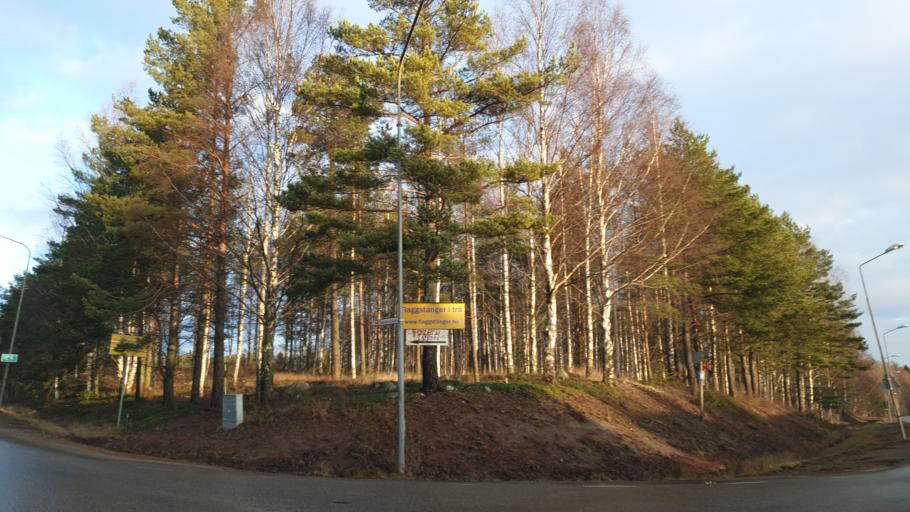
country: SE
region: Gaevleborg
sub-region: Hudiksvalls Kommun
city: Hudiksvall
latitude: 61.7243
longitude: 17.1448
